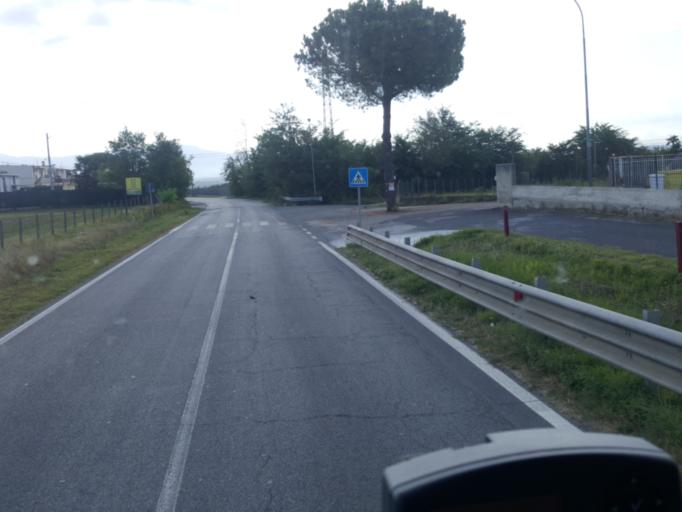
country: IT
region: Latium
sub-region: Citta metropolitana di Roma Capitale
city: Bivio di Capanelle
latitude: 42.1247
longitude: 12.5769
